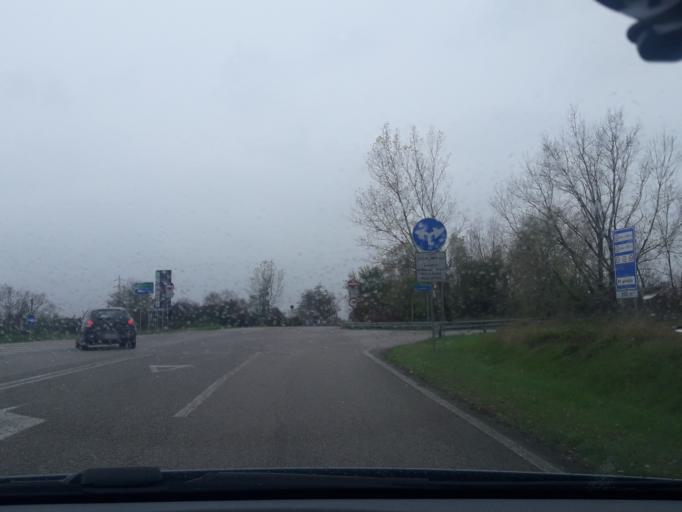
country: IT
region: Friuli Venezia Giulia
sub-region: Provincia di Udine
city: Basaldella
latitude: 46.0458
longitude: 13.2103
